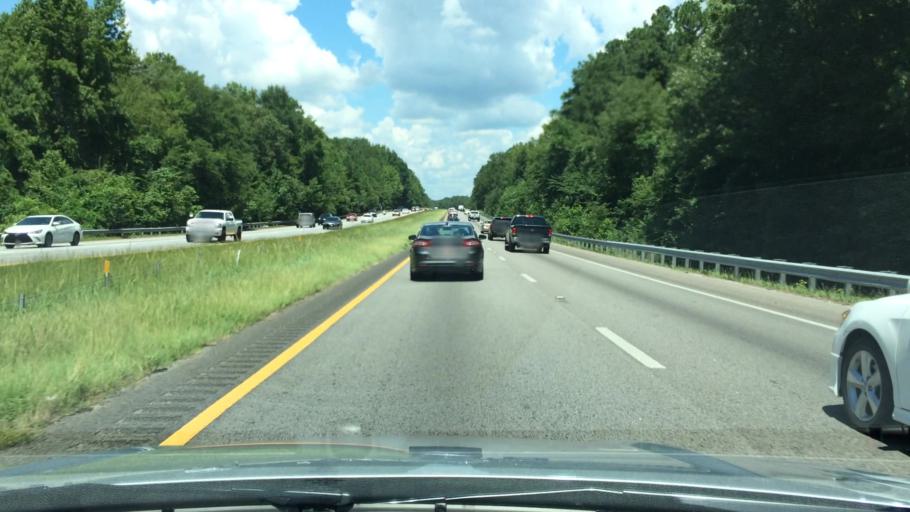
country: US
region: South Carolina
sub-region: Lexington County
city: Irmo
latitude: 34.1252
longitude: -81.2018
